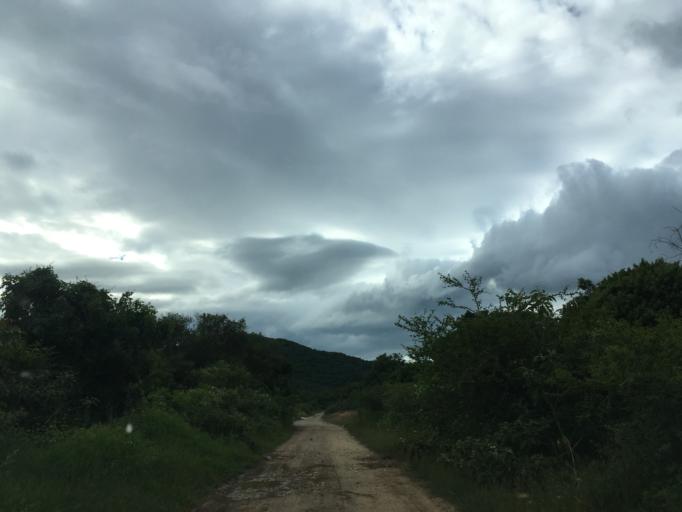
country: MX
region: Guanajuato
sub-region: Acambaro
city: La Ortiga
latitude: 19.9778
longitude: -100.9627
